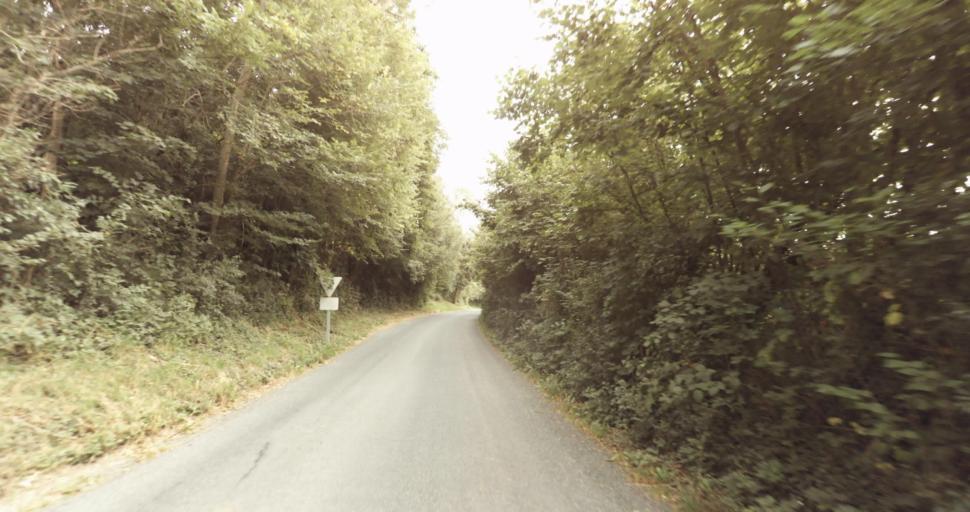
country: FR
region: Haute-Normandie
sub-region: Departement de l'Eure
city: Saint-Germain-sur-Avre
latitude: 48.7783
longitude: 1.2582
